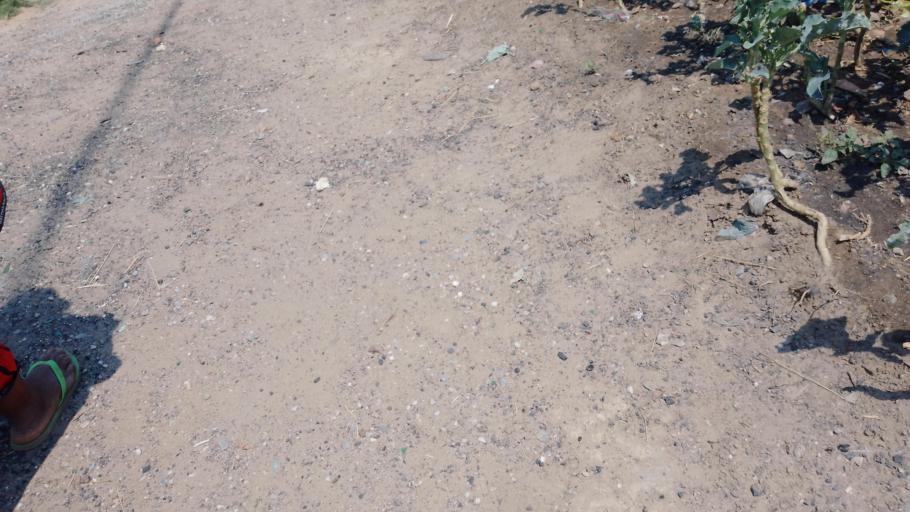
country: ZM
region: Lusaka
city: Lusaka
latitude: -15.3978
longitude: 28.3676
